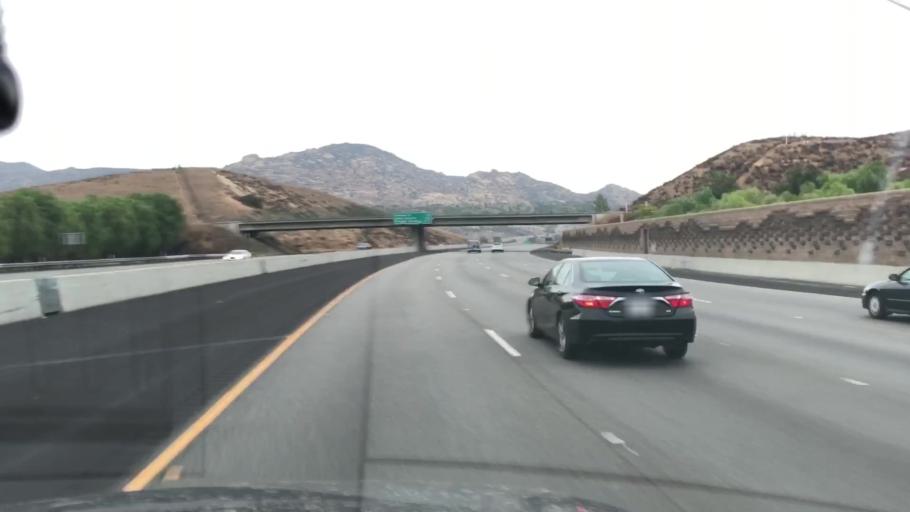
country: US
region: California
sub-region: Ventura County
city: Santa Susana
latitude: 34.2814
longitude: -118.6733
